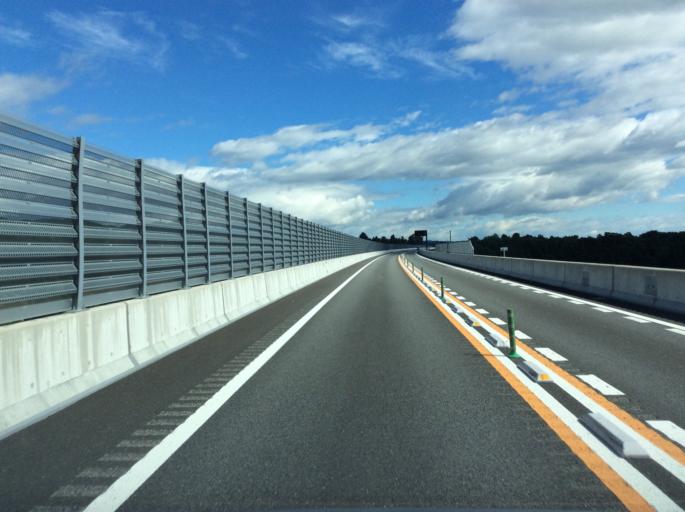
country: JP
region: Fukushima
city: Namie
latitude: 37.5954
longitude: 140.9269
